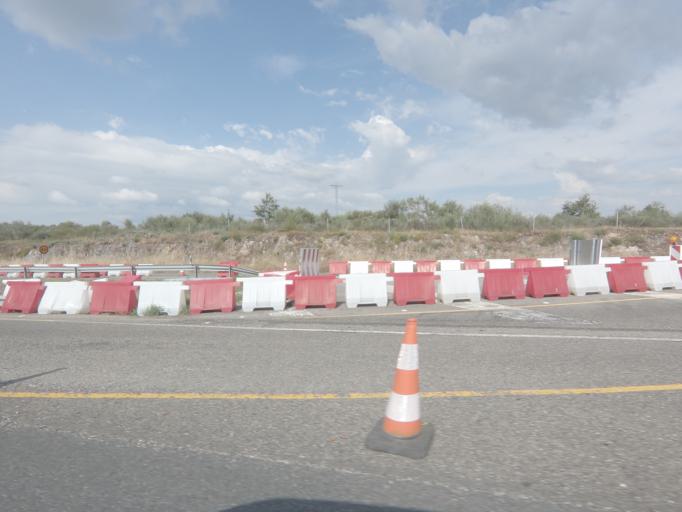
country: ES
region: Galicia
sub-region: Provincia de Ourense
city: Taboadela
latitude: 42.2408
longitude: -7.8592
